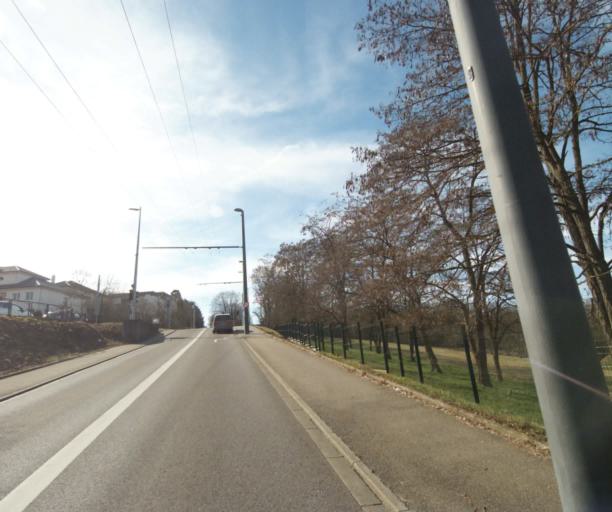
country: FR
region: Lorraine
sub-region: Departement de Meurthe-et-Moselle
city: Villers-les-Nancy
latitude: 48.6594
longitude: 6.1586
